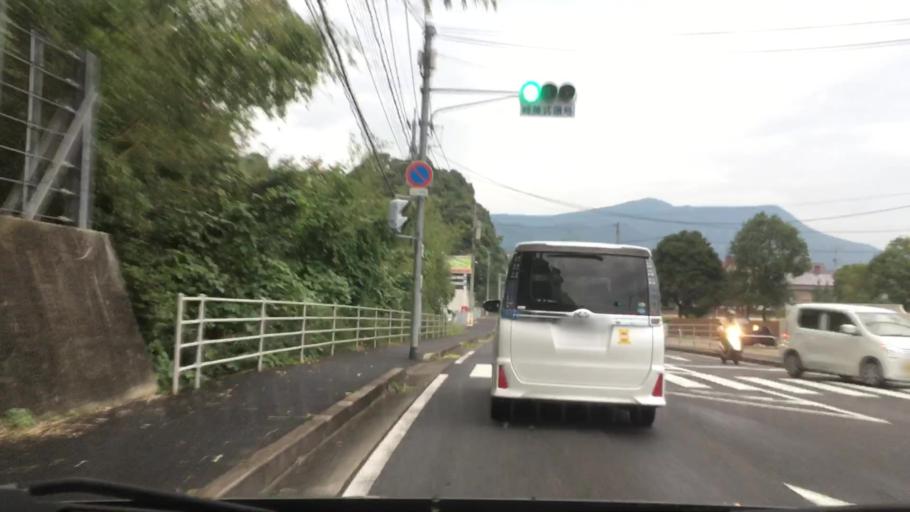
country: JP
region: Nagasaki
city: Sasebo
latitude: 33.1267
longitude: 129.7922
